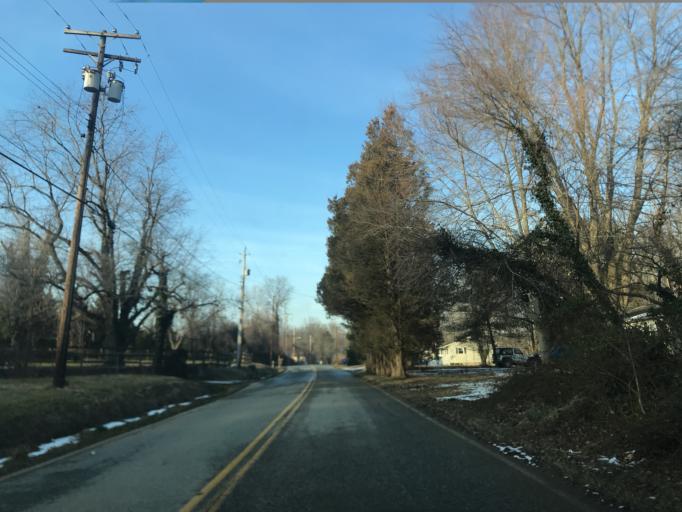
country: US
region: Maryland
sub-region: Harford County
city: Edgewood
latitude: 39.4039
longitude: -76.3249
